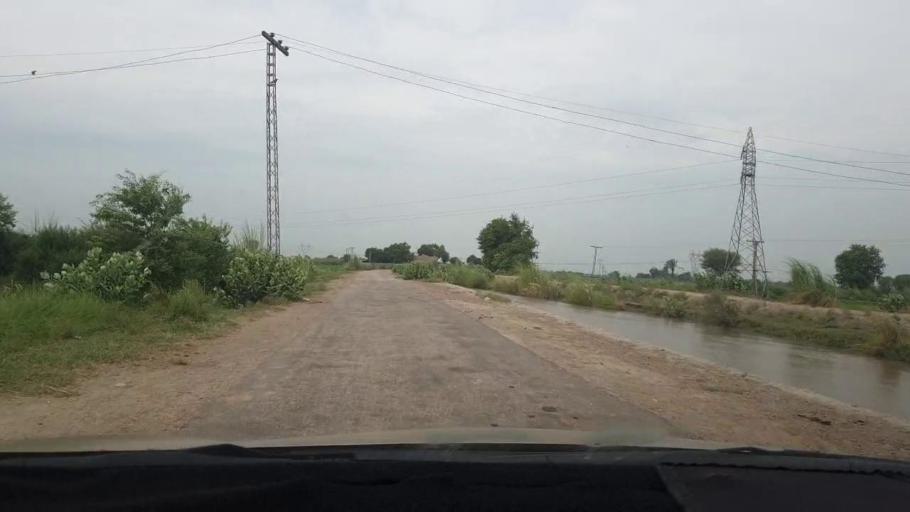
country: PK
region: Sindh
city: Naudero
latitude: 27.6793
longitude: 68.3469
